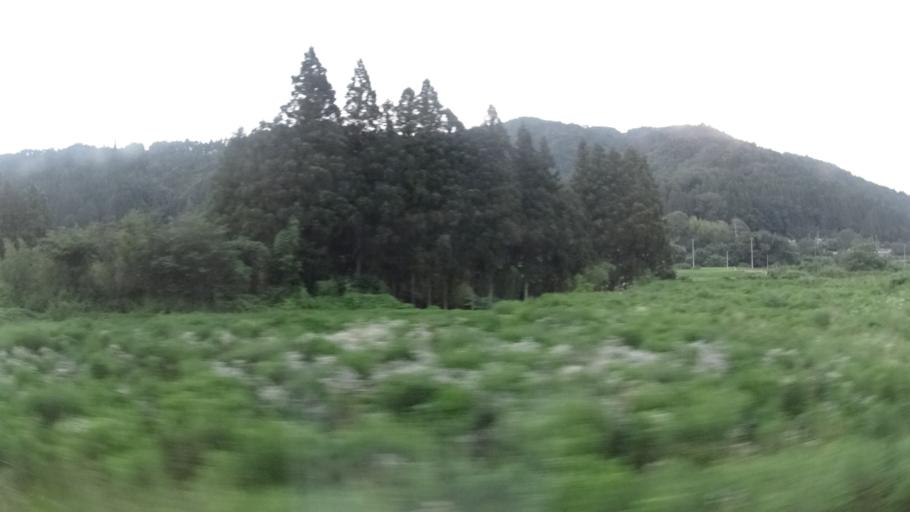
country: JP
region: Fukushima
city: Iwaki
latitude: 37.2028
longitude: 140.7569
